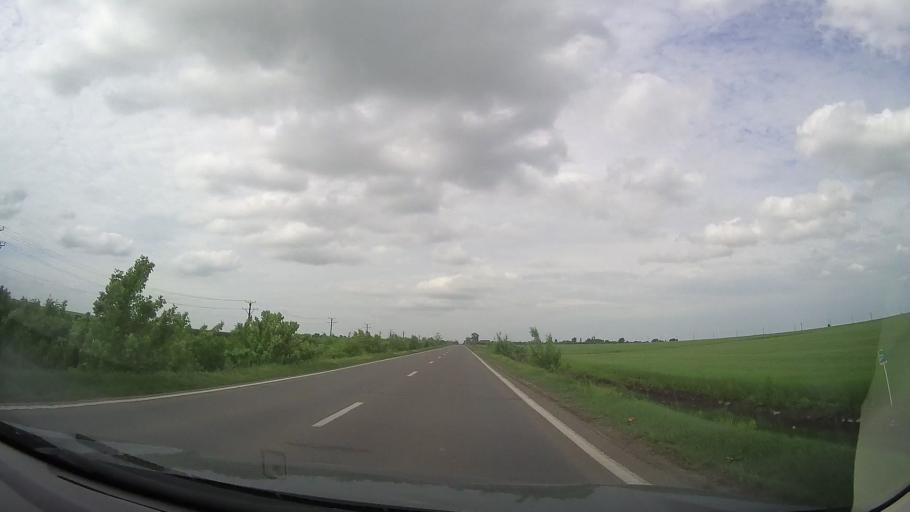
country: RO
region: Teleorman
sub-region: Comuna Draganesti-Vlasca
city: Draganesti-Vlasca
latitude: 44.0737
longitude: 25.5460
